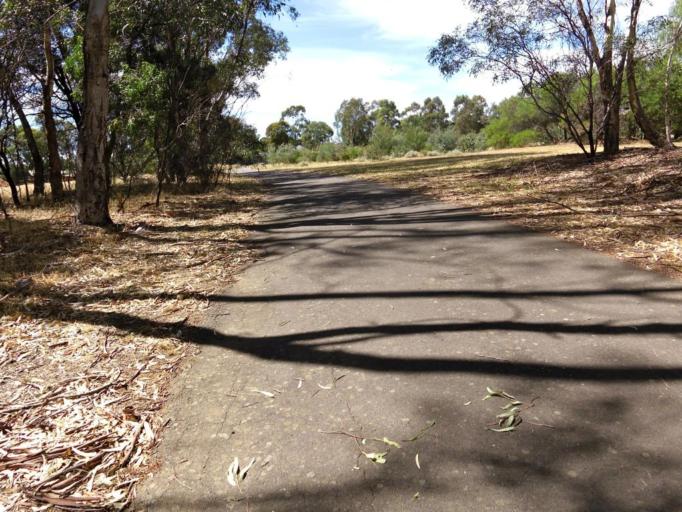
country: AU
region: Victoria
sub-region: Greater Bendigo
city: White Hills
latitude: -36.7403
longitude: 144.2947
